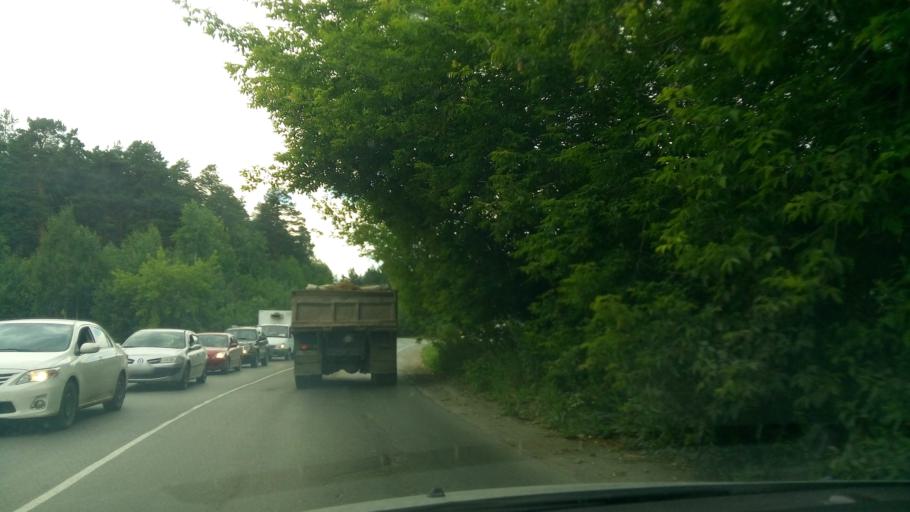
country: RU
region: Sverdlovsk
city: Yekaterinburg
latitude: 56.8850
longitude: 60.6817
